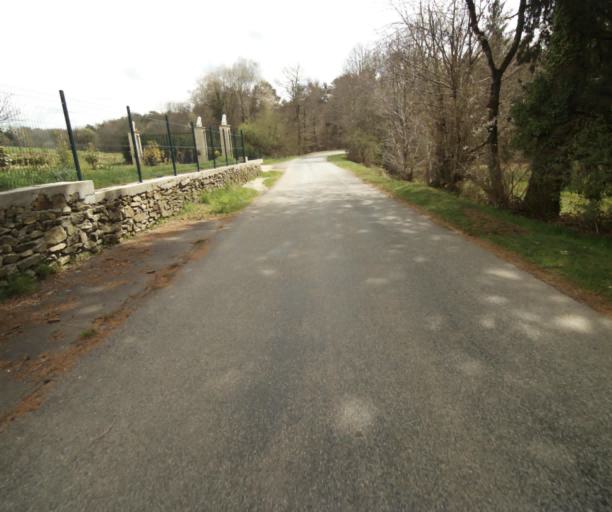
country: FR
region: Limousin
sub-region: Departement de la Correze
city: Laguenne
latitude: 45.2168
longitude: 1.8962
